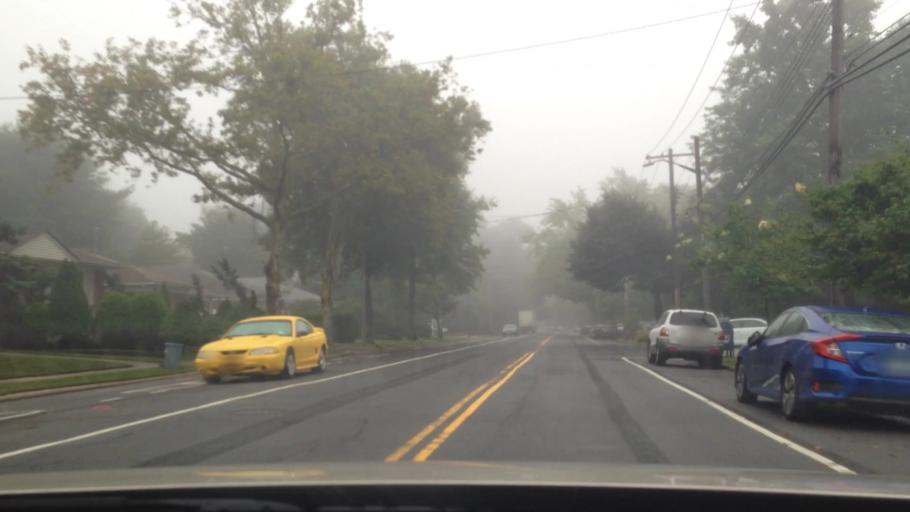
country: US
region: New York
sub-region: Nassau County
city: Great Neck Estates
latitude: 40.7553
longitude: -73.7484
